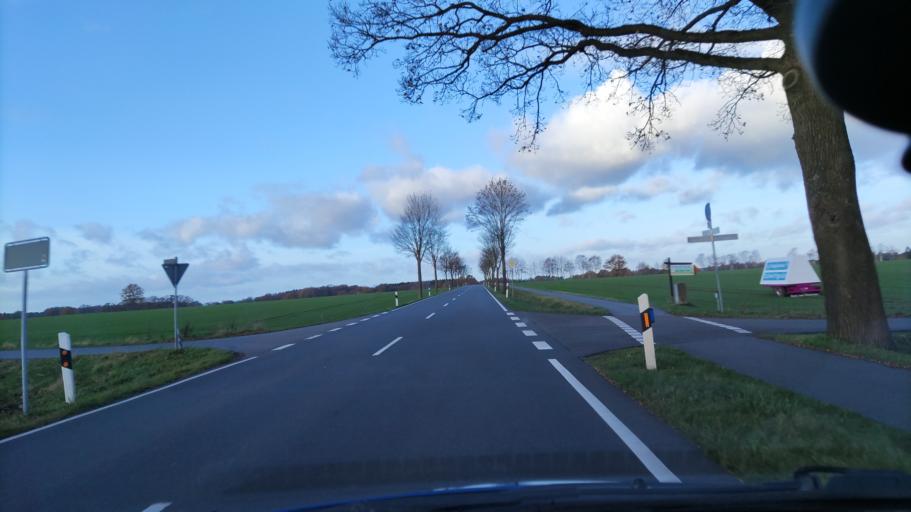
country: DE
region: Lower Saxony
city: Schneverdingen
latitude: 53.0624
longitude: 9.8177
